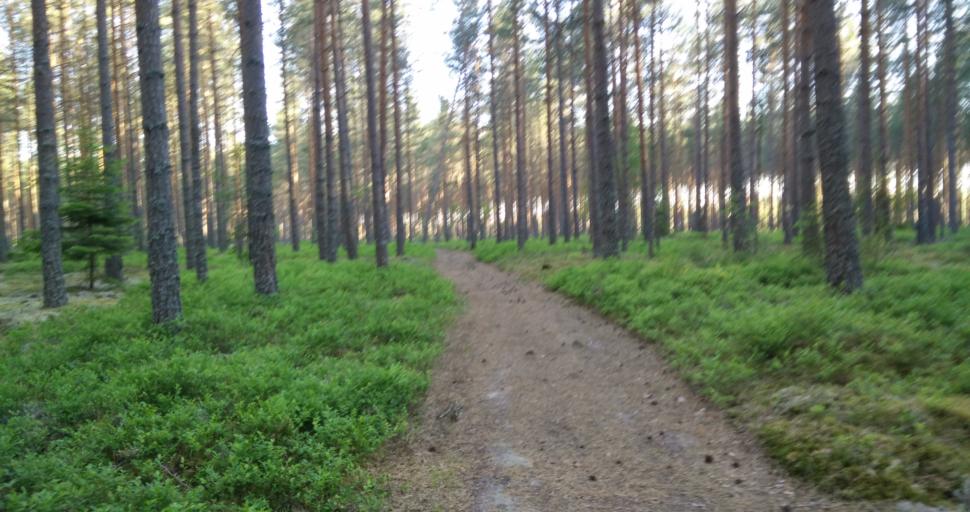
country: SE
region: Vaermland
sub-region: Hagfors Kommun
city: Hagfors
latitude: 60.0175
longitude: 13.5863
